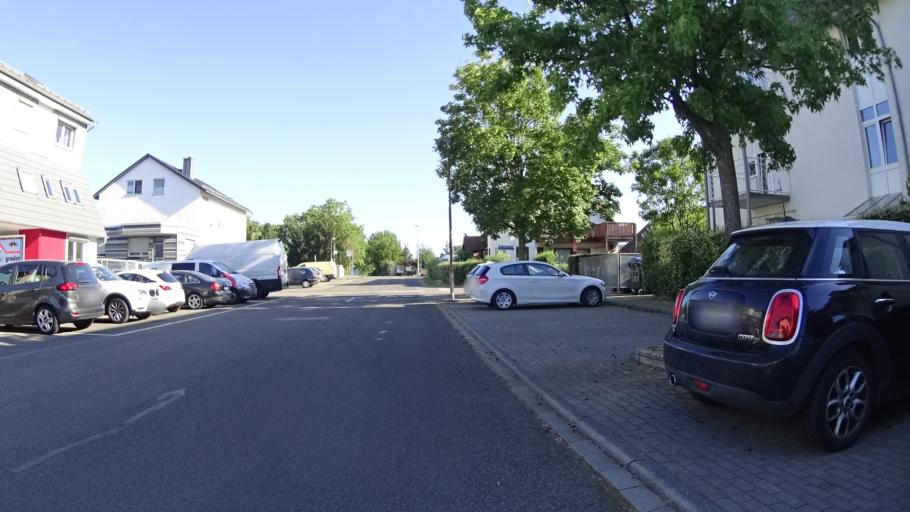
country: DE
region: Baden-Wuerttemberg
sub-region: Karlsruhe Region
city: Laudenbach
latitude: 49.6106
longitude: 8.6416
